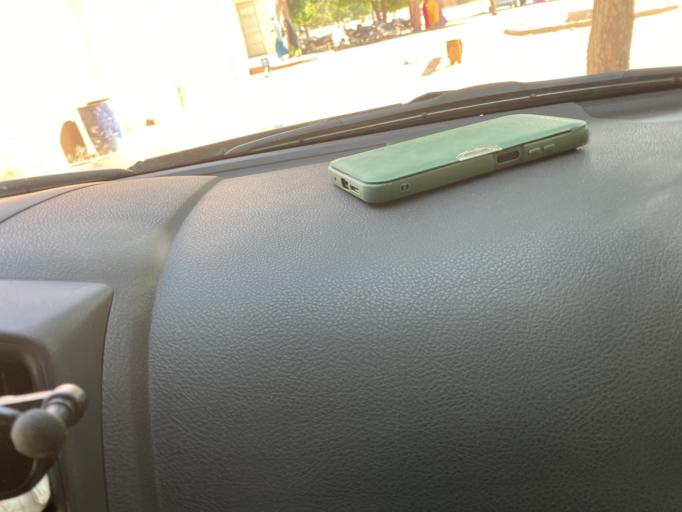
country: NE
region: Maradi
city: Guidan Roumdji
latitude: 13.6583
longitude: 6.6865
